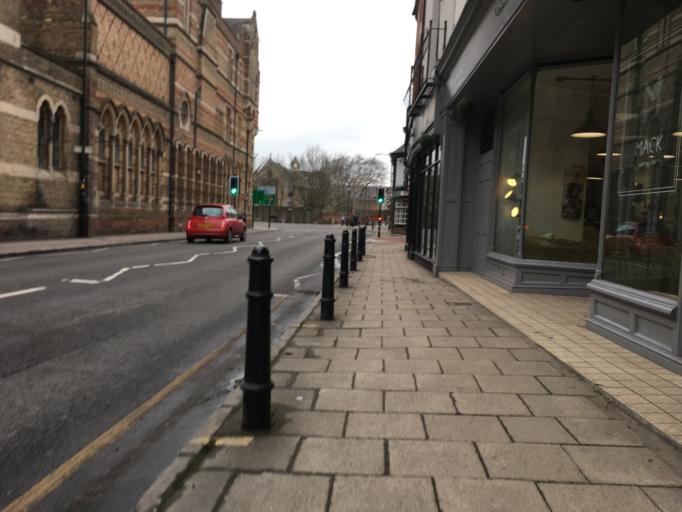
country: GB
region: England
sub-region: Warwickshire
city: Rugby
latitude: 52.3708
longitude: -1.2632
